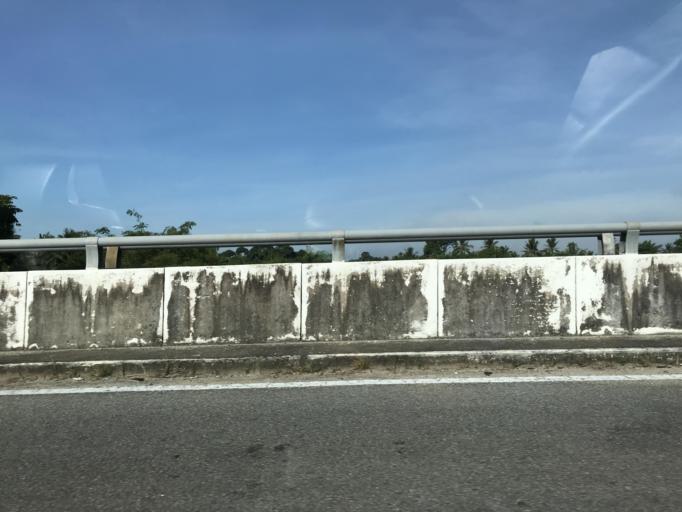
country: MY
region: Kelantan
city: Kampong Kadok
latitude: 6.0540
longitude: 102.2154
